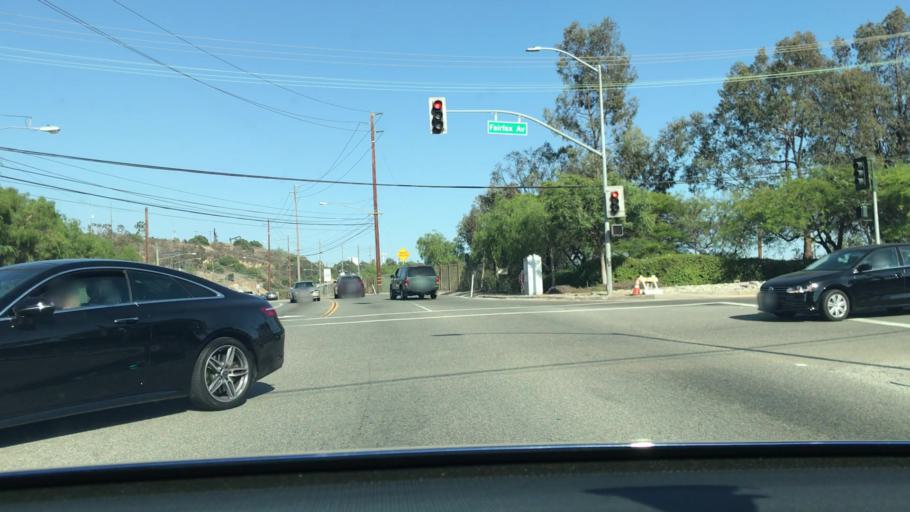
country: US
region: California
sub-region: Los Angeles County
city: Ladera Heights
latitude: 33.9983
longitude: -118.3655
